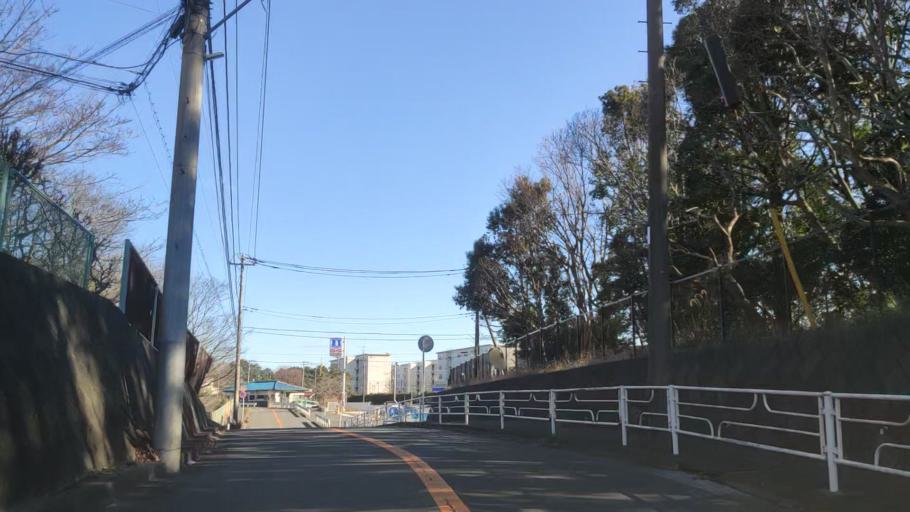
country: JP
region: Kanagawa
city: Minami-rinkan
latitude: 35.5035
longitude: 139.5280
